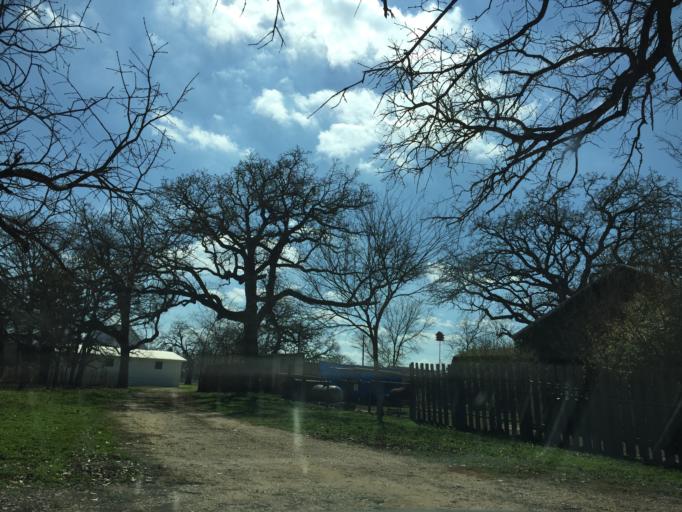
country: US
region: Texas
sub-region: Milam County
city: Thorndale
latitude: 30.5589
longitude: -97.1757
